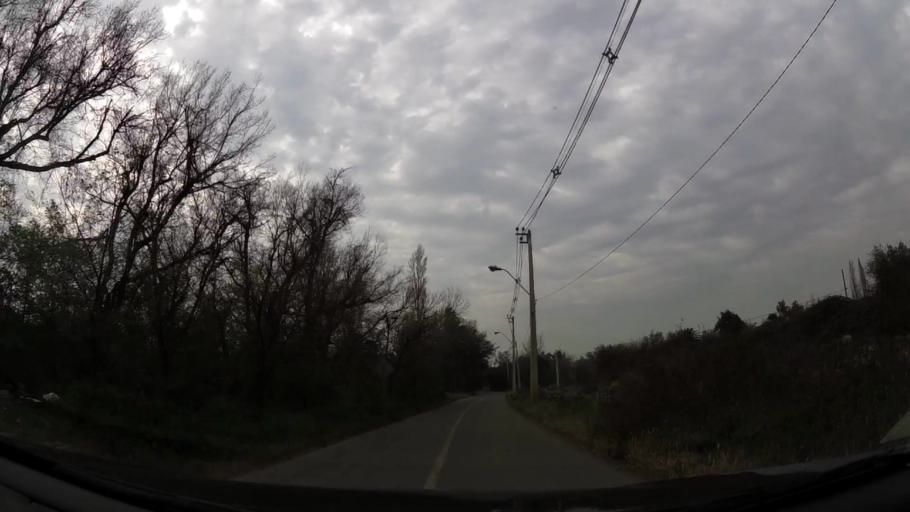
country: CL
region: Santiago Metropolitan
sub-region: Provincia de Chacabuco
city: Lampa
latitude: -33.2235
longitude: -70.7710
